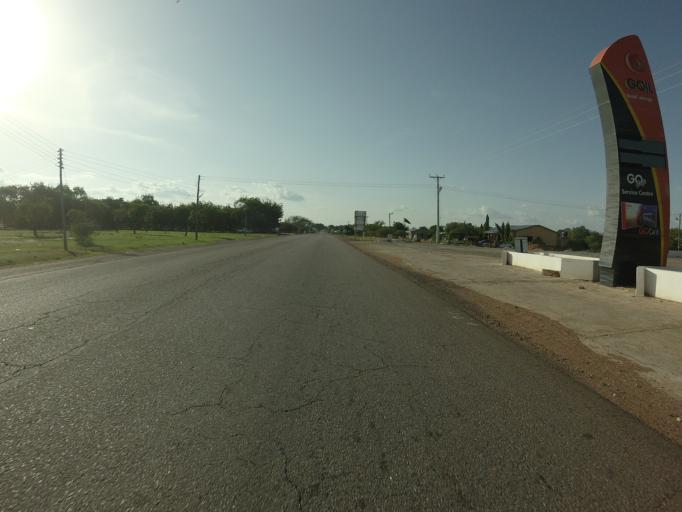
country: GH
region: Upper East
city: Navrongo
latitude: 10.9574
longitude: -1.0978
